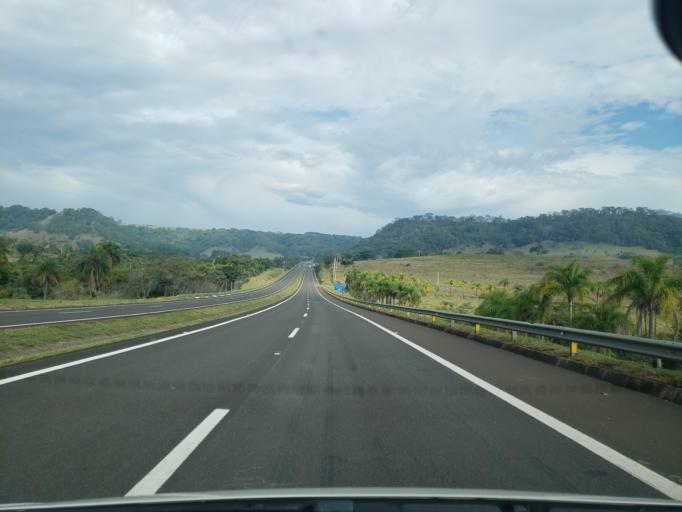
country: BR
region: Sao Paulo
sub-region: Dois Corregos
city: Dois Corregos
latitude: -22.2441
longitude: -48.3249
